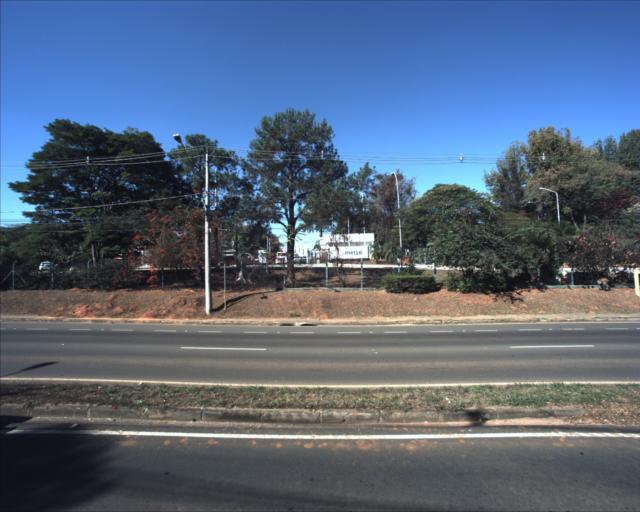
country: BR
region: Sao Paulo
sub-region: Sorocaba
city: Sorocaba
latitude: -23.4426
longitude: -47.4169
